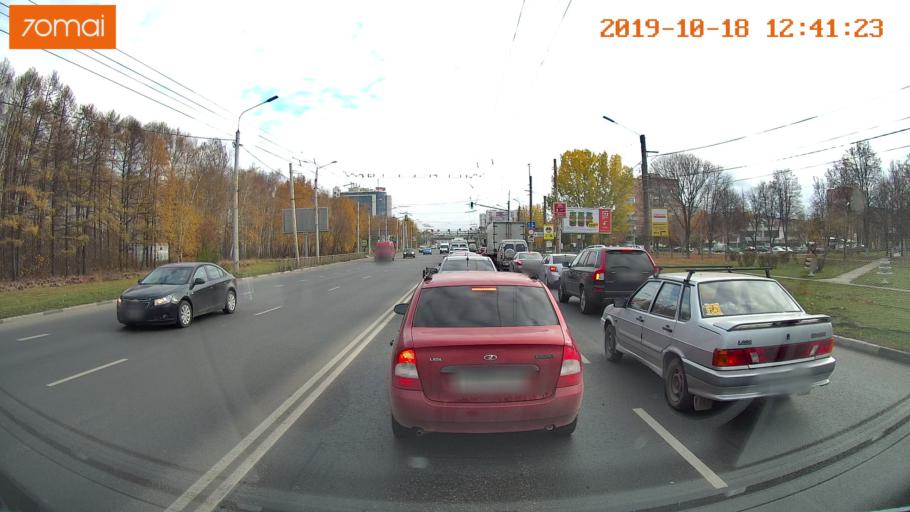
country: RU
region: Rjazan
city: Ryazan'
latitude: 54.6459
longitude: 39.6571
